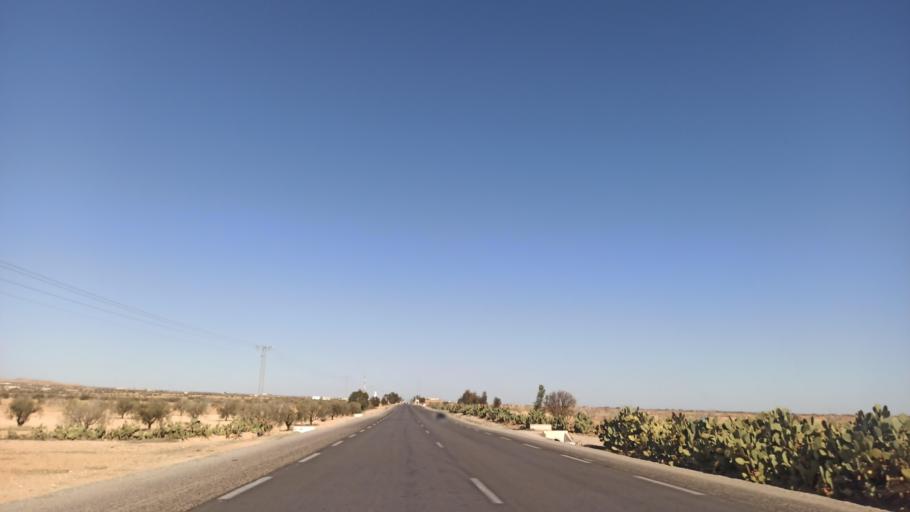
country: TN
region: Sidi Bu Zayd
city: Bi'r al Hufayy
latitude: 34.7334
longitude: 9.0687
